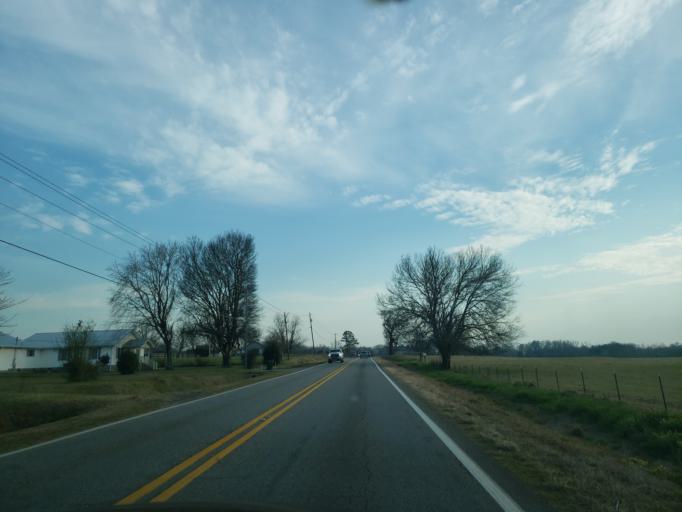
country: US
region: Alabama
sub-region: Hale County
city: Moundville
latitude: 32.9752
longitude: -87.6245
